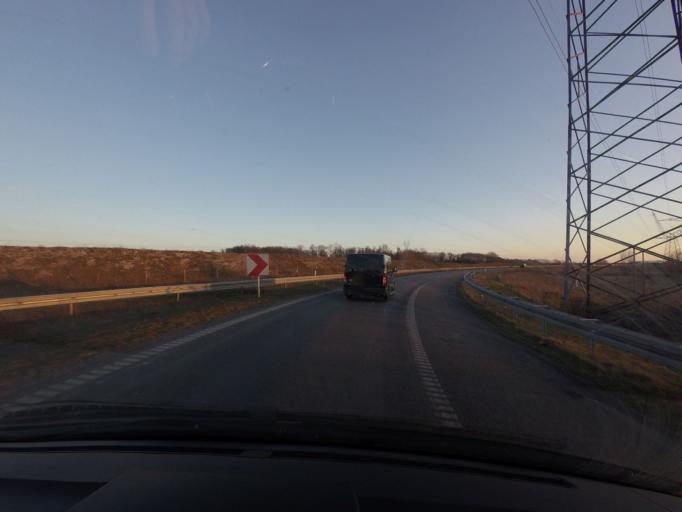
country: DK
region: South Denmark
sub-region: Odense Kommune
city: Neder Holluf
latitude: 55.3493
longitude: 10.4598
